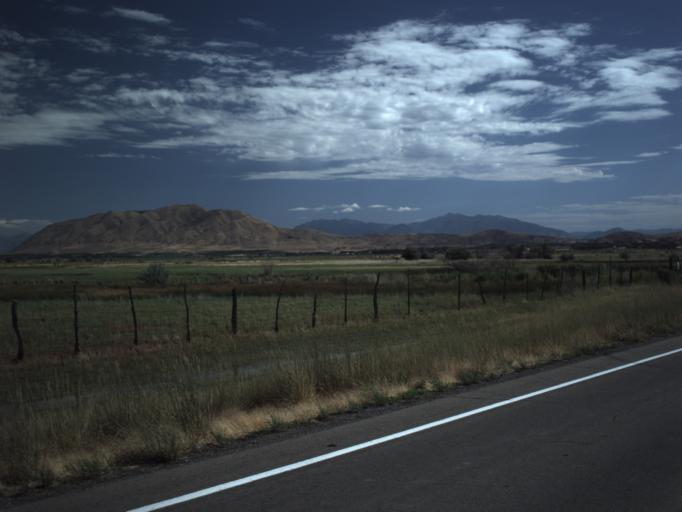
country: US
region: Utah
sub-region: Utah County
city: Genola
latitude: 39.9536
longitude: -111.8921
